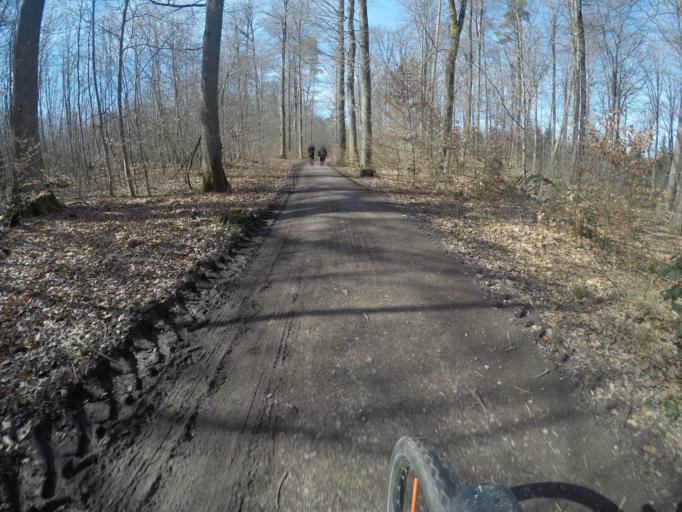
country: DE
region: Baden-Wuerttemberg
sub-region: Regierungsbezirk Stuttgart
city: Gerlingen
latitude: 48.7745
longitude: 9.0698
